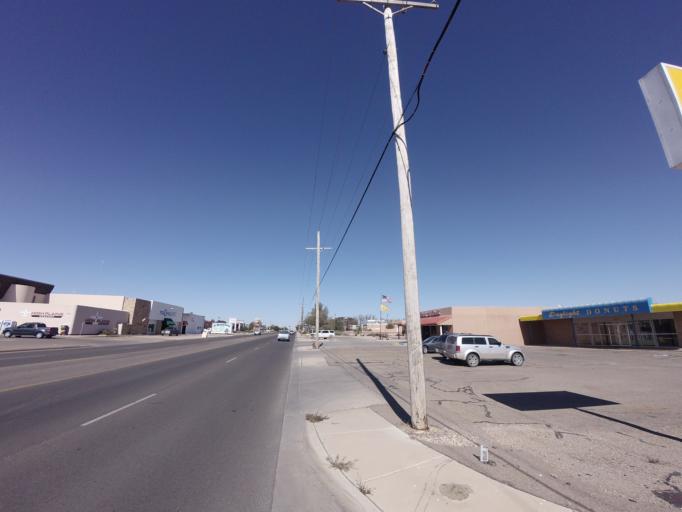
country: US
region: New Mexico
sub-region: Curry County
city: Clovis
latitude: 34.4217
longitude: -103.1964
